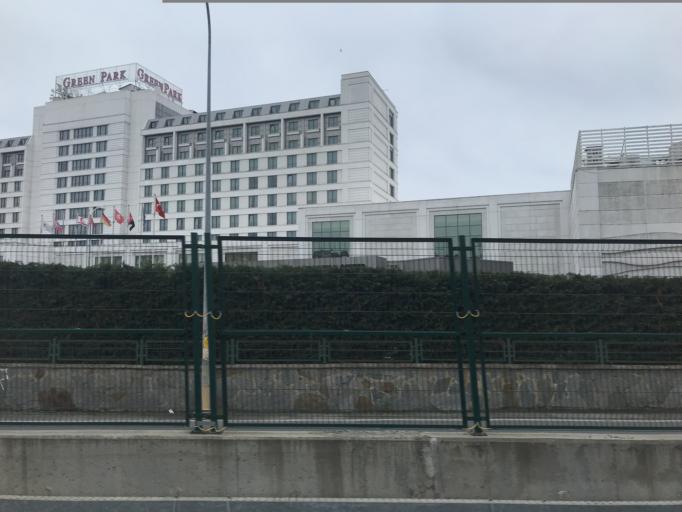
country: TR
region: Istanbul
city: Pendik
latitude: 40.8738
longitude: 29.2510
